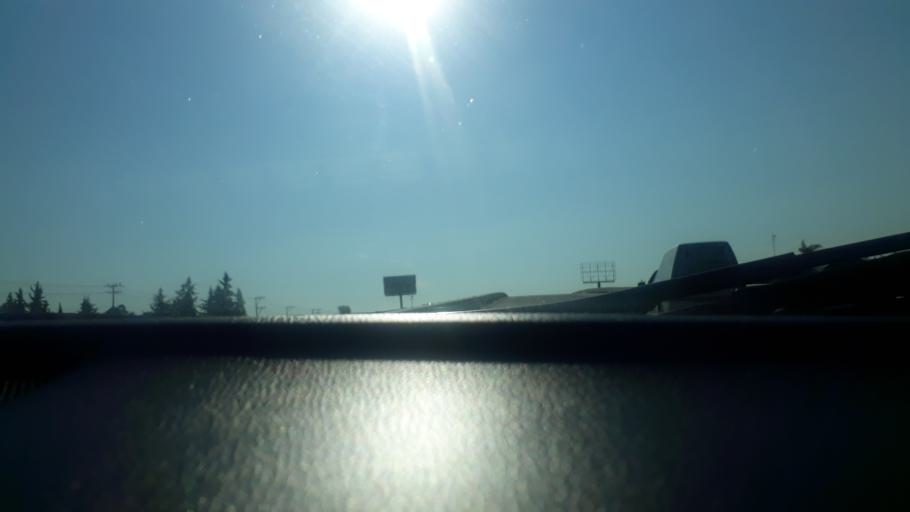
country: MX
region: Puebla
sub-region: Puebla
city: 18 de Marzo
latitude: 18.9724
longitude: -98.1951
